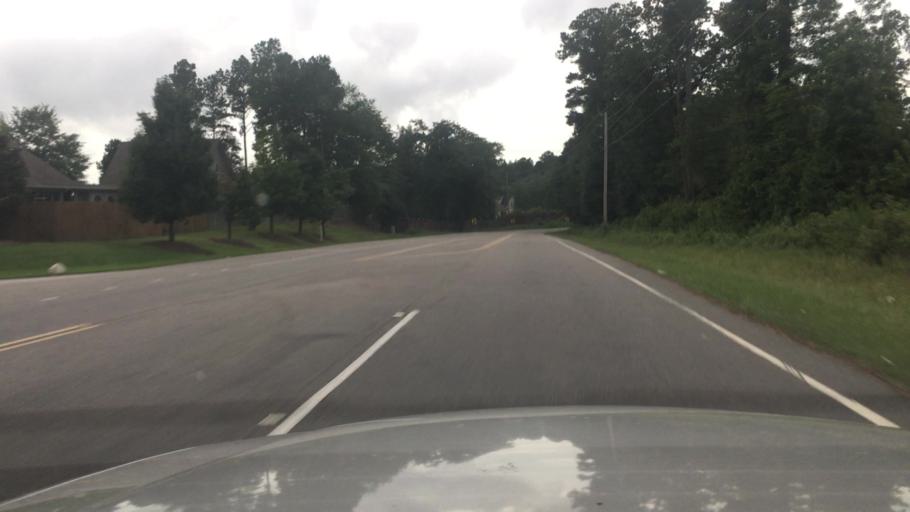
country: US
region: North Carolina
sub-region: Hoke County
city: Rockfish
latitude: 34.9597
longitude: -79.0346
